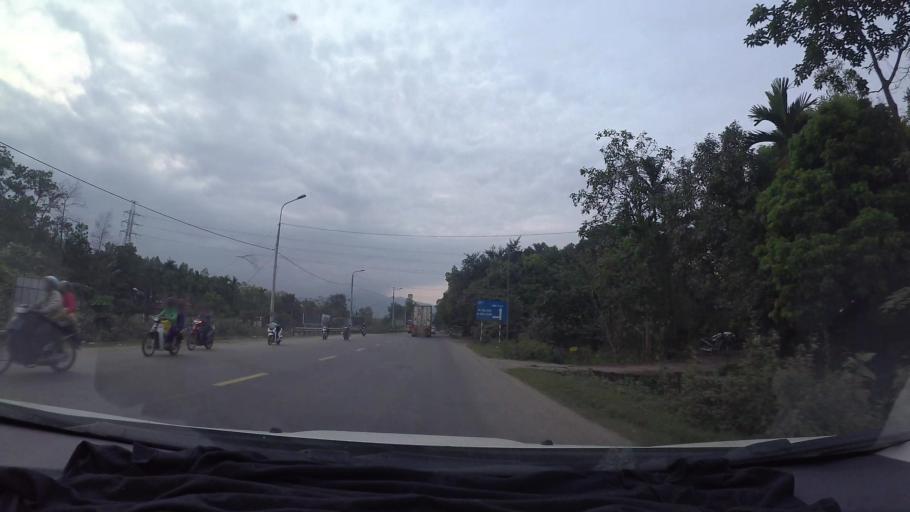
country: VN
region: Da Nang
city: Lien Chieu
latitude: 16.0556
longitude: 108.1014
